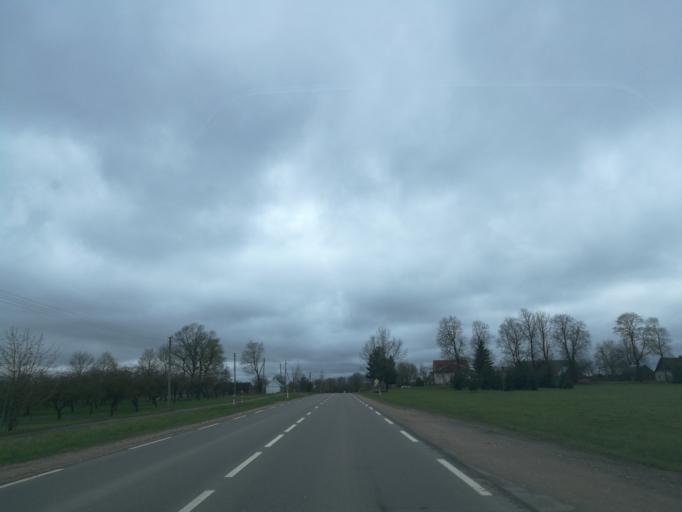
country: LT
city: Raseiniai
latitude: 55.4024
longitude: 23.1555
